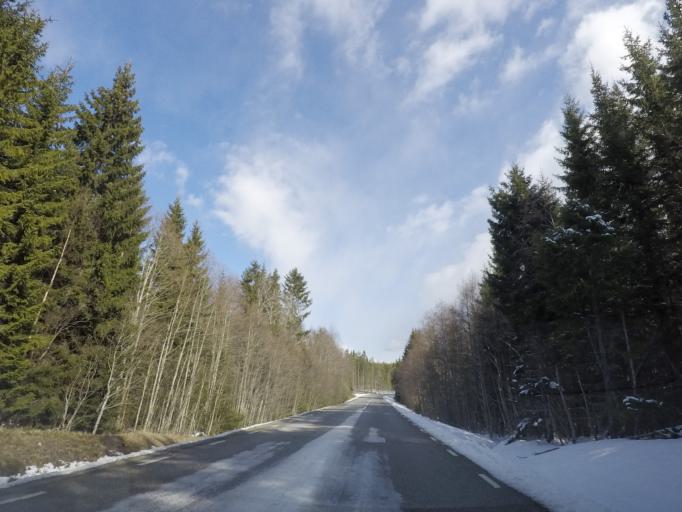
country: SE
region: OErebro
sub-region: Lindesbergs Kommun
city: Stora
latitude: 59.9013
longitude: 15.2080
